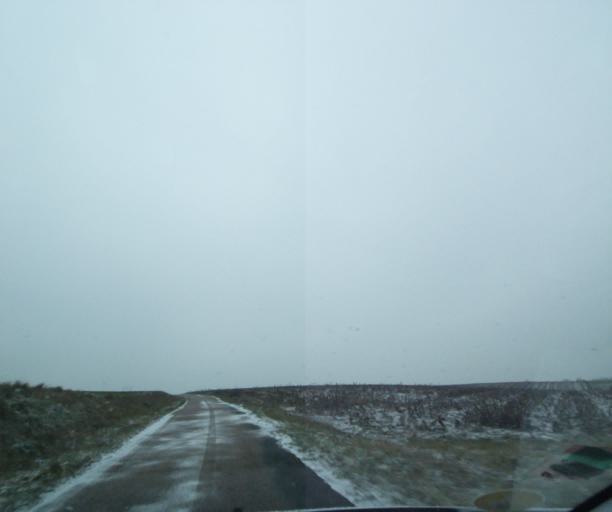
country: FR
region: Champagne-Ardenne
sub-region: Departement de la Haute-Marne
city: Wassy
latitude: 48.4663
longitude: 5.0054
